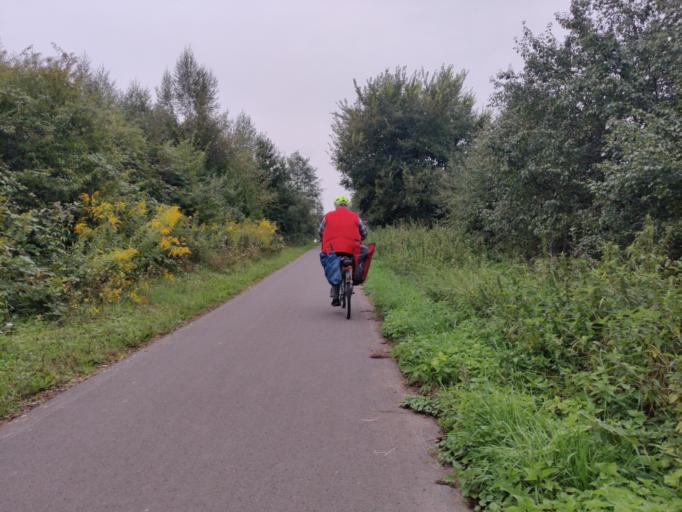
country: DE
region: Lower Saxony
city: Heinsen
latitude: 51.9026
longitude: 9.4498
